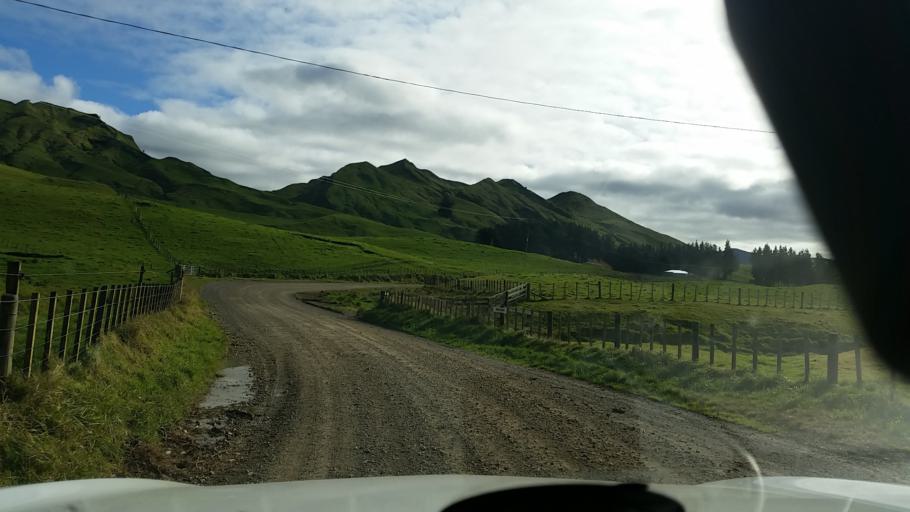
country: NZ
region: Hawke's Bay
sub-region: Napier City
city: Napier
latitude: -39.1270
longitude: 176.8954
